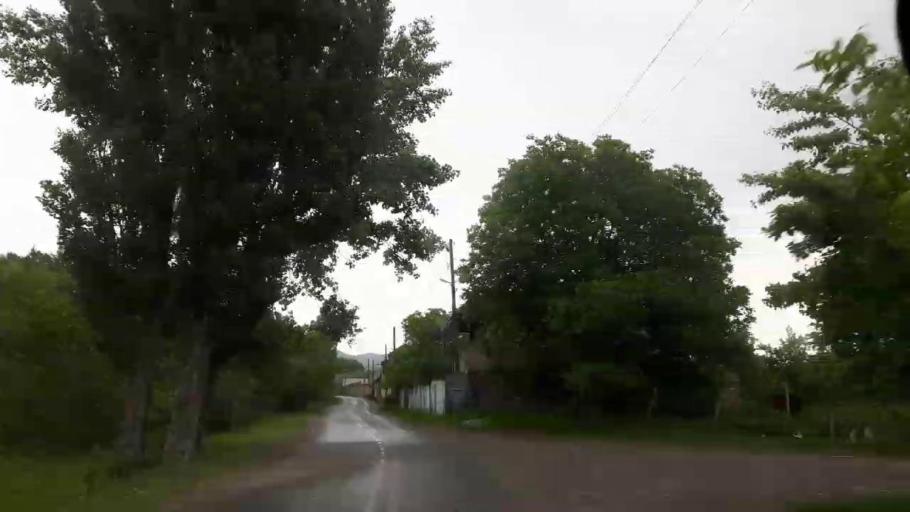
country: GE
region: Shida Kartli
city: Gori
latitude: 41.9632
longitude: 44.2208
